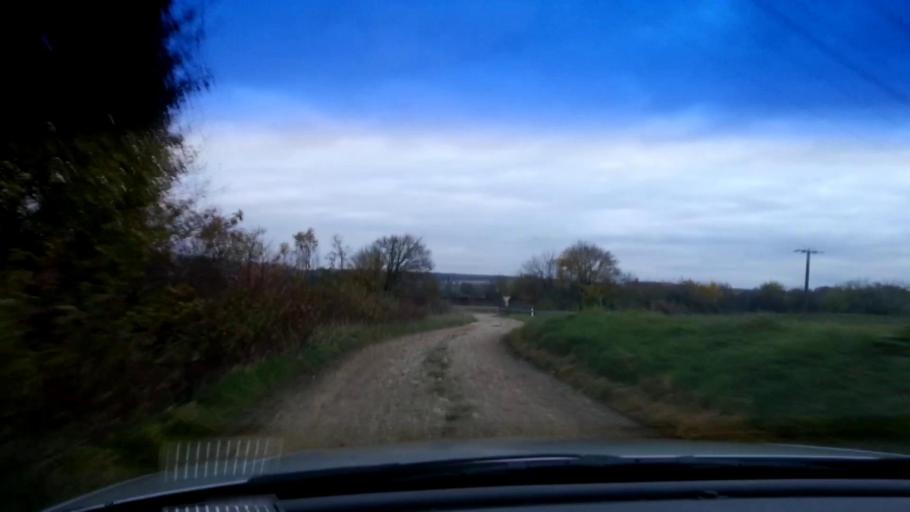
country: DE
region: Bavaria
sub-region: Upper Franconia
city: Schesslitz
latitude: 49.9672
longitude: 10.9947
